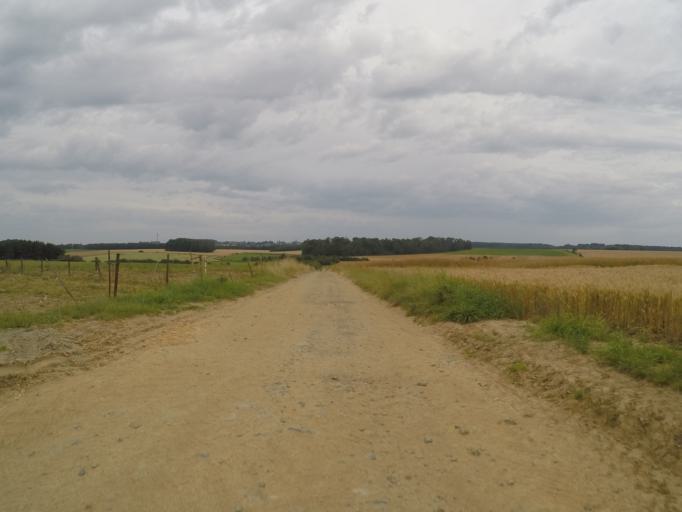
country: BE
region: Wallonia
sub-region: Province de Namur
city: Assesse
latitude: 50.3038
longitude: 4.9999
